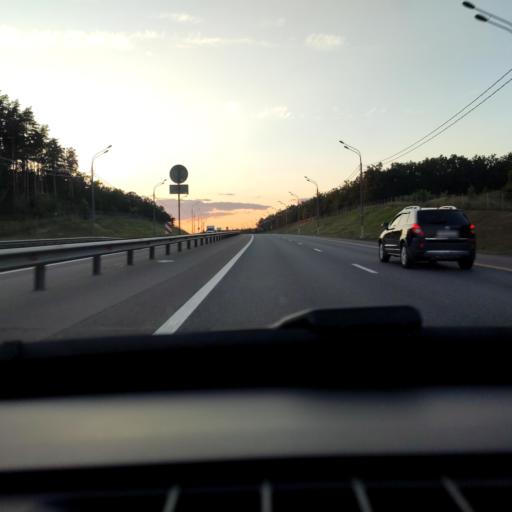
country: RU
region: Lipetsk
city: Khlevnoye
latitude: 52.3124
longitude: 39.0452
